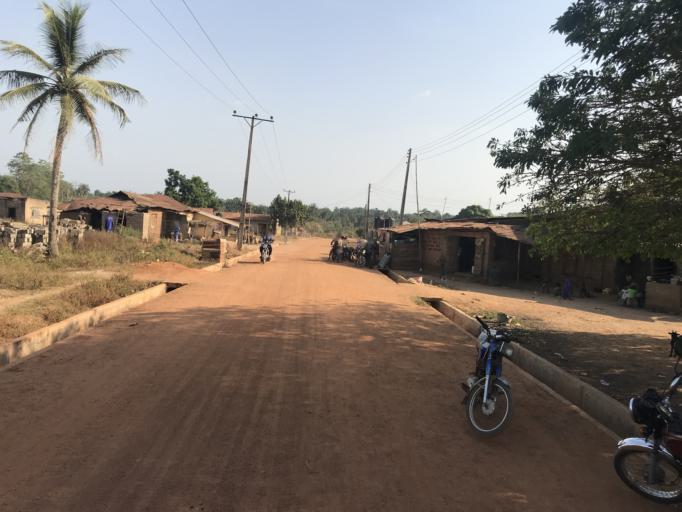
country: NG
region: Osun
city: Inisa
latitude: 7.8119
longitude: 4.2790
